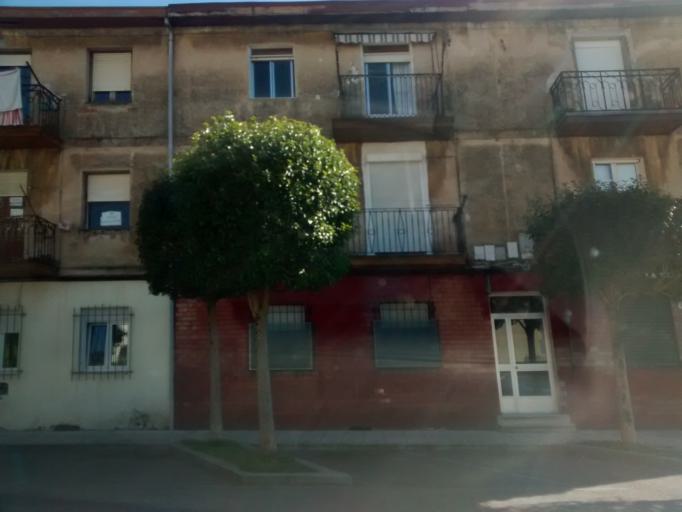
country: ES
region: Cantabria
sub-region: Provincia de Cantabria
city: Santander
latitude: 43.4563
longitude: -3.8214
